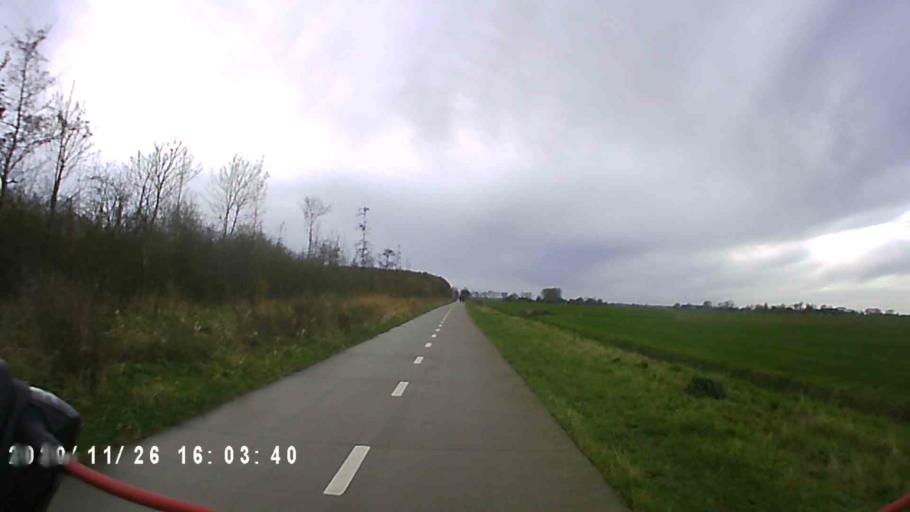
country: NL
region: Groningen
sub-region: Gemeente Bedum
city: Bedum
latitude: 53.2715
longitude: 6.6817
